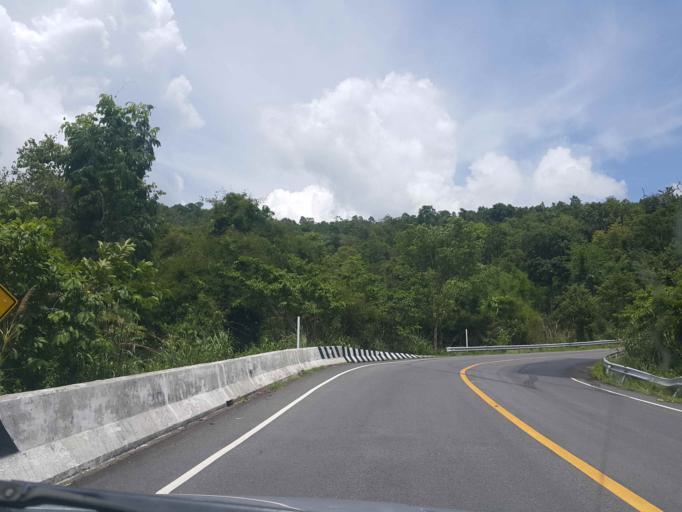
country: TH
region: Phayao
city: Chiang Muan
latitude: 18.8434
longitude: 100.3510
